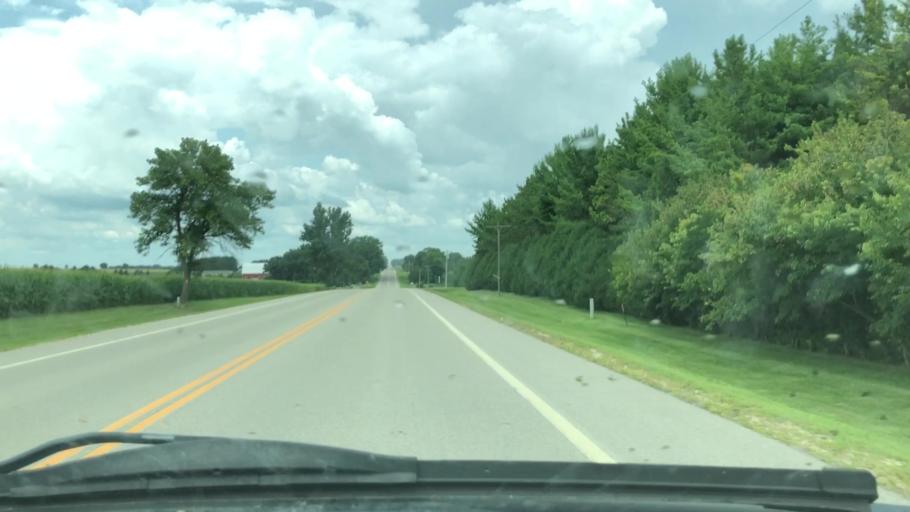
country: US
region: Minnesota
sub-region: Olmsted County
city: Stewartville
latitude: 43.8677
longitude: -92.5286
